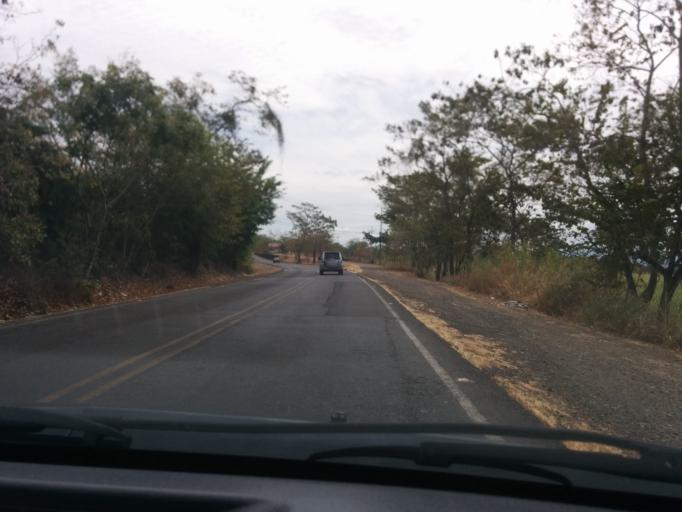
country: CR
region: Puntarenas
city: Esparza
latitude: 10.0039
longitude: -84.6263
